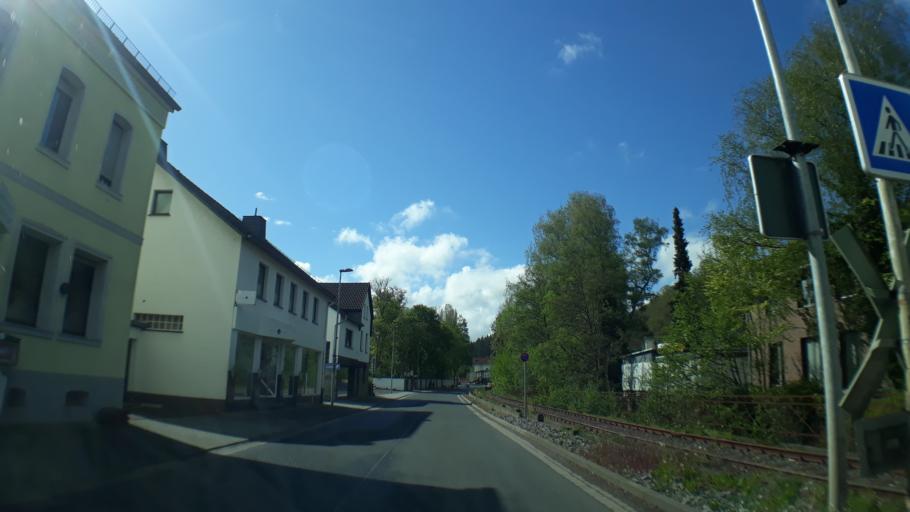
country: DE
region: North Rhine-Westphalia
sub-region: Regierungsbezirk Koln
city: Hellenthal
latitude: 50.4891
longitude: 6.4470
